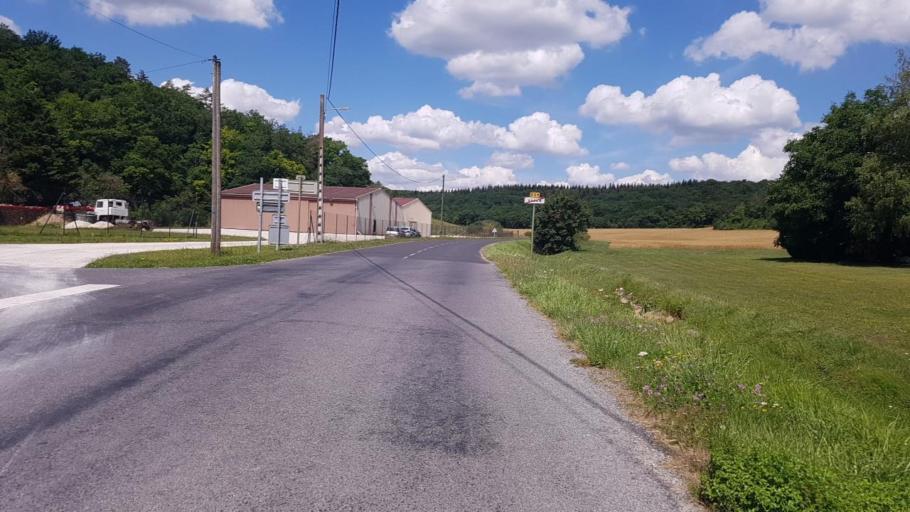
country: FR
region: Lorraine
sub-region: Departement de la Meuse
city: Vacon
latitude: 48.6691
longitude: 5.6001
